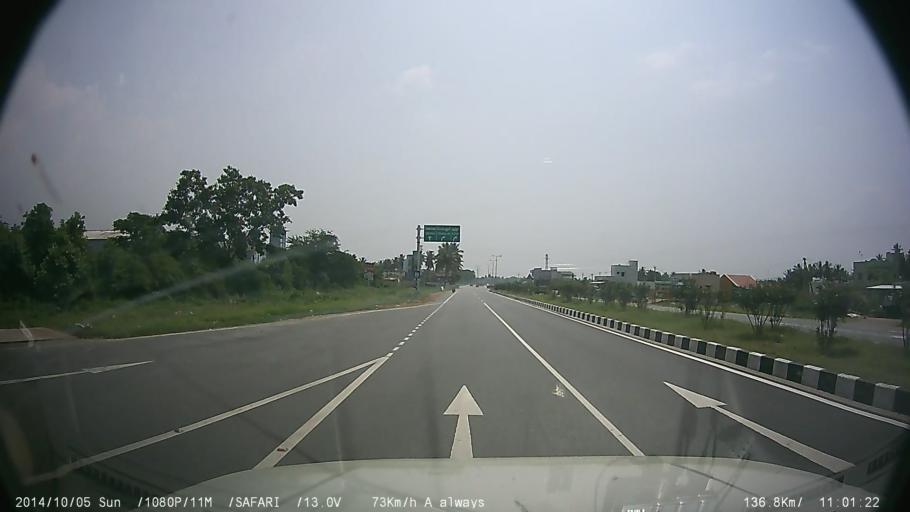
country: IN
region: Tamil Nadu
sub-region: Salem
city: Attur
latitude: 11.6172
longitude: 78.5581
